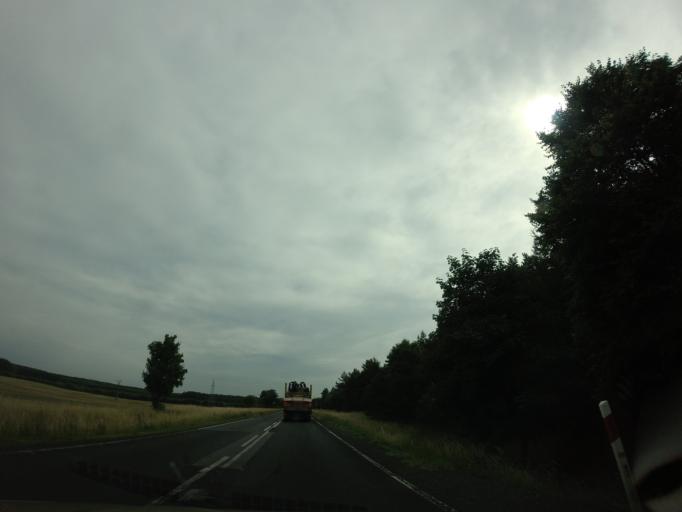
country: PL
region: West Pomeranian Voivodeship
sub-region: Powiat drawski
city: Kalisz Pomorski
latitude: 53.3080
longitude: 15.9871
